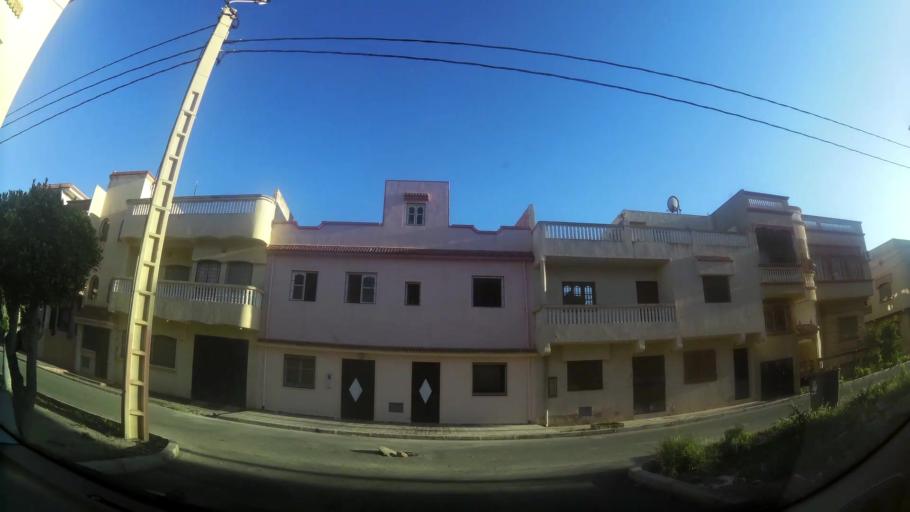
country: MA
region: Oriental
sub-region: Berkane-Taourirt
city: Madagh
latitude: 35.0829
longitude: -2.2385
